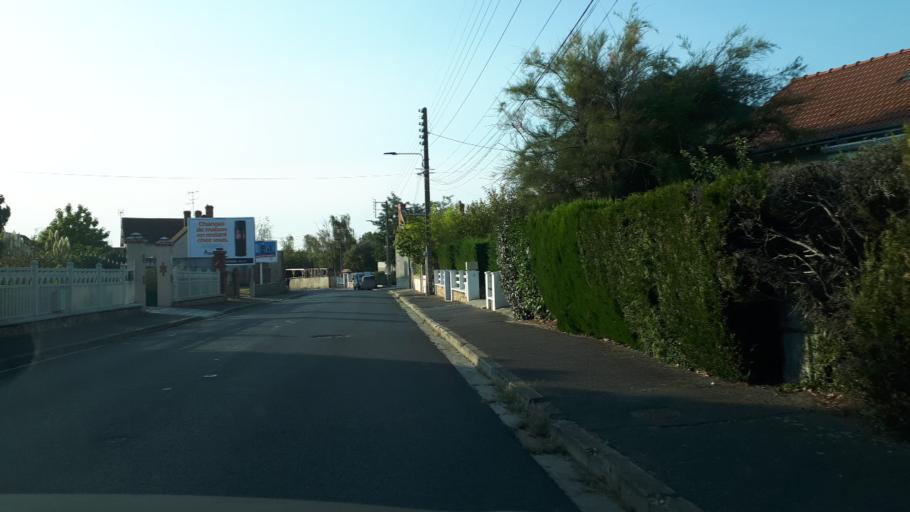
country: FR
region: Centre
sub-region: Departement du Loir-et-Cher
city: Romorantin-Lanthenay
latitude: 47.3511
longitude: 1.7527
